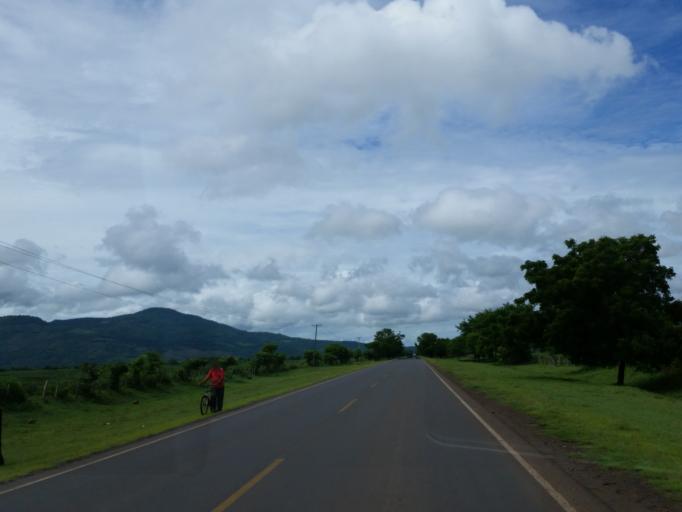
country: NI
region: Leon
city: Larreynaga
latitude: 12.6009
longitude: -86.6884
